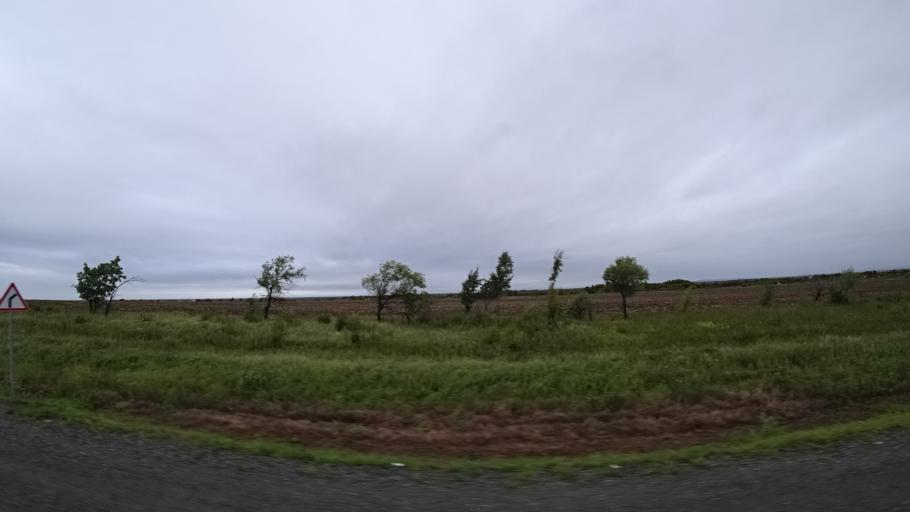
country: RU
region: Primorskiy
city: Chernigovka
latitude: 44.3187
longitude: 132.5653
